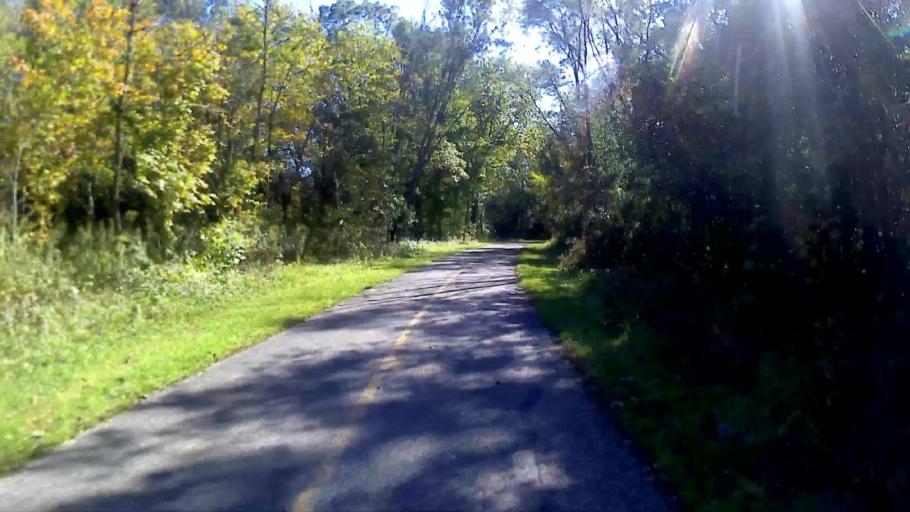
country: US
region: Illinois
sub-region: Cook County
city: Elk Grove Village
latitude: 42.0220
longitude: -87.9912
